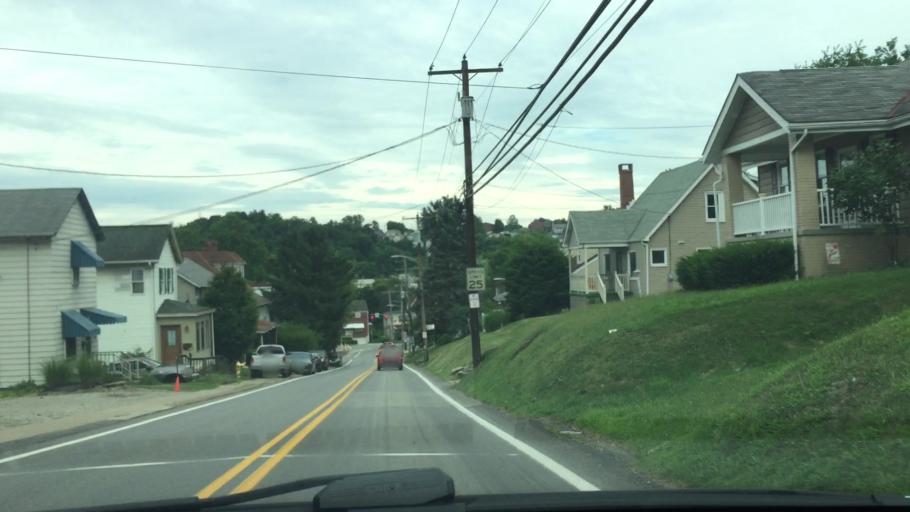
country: US
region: Pennsylvania
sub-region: Allegheny County
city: Bridgeville
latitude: 40.3633
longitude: -80.1123
